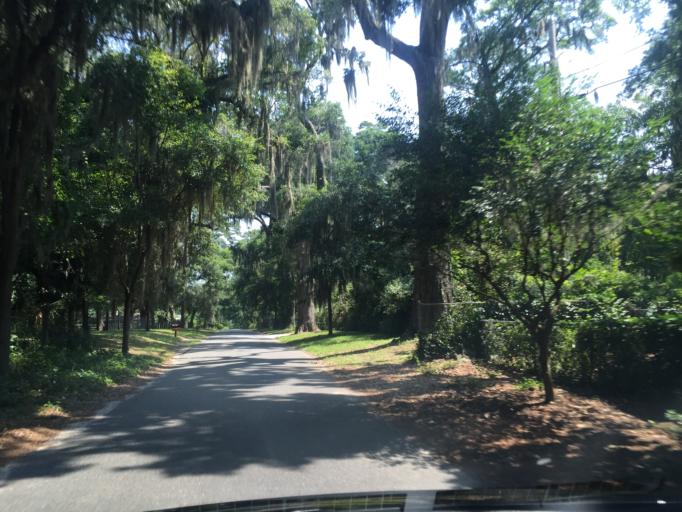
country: US
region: Georgia
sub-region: Chatham County
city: Montgomery
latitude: 31.9645
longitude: -81.1265
